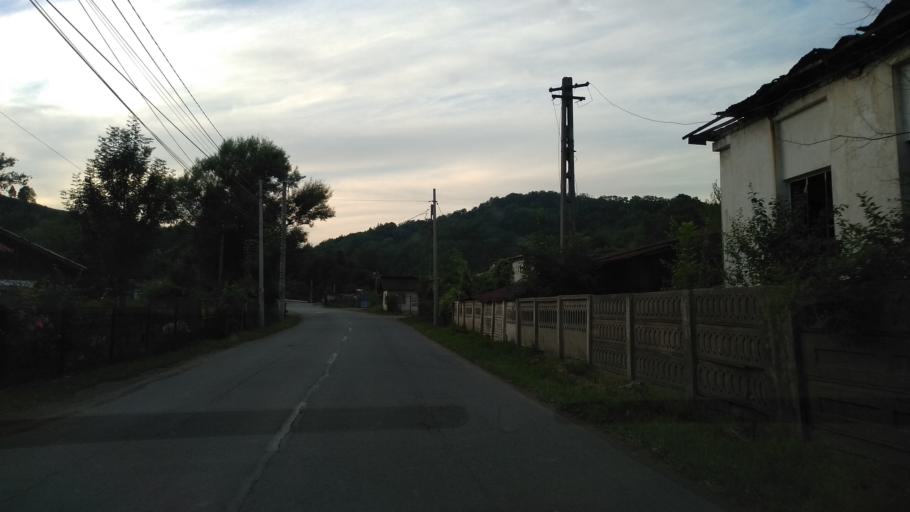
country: RO
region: Hunedoara
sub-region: Comuna Aninoasa
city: Iscroni
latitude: 45.3835
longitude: 23.3286
